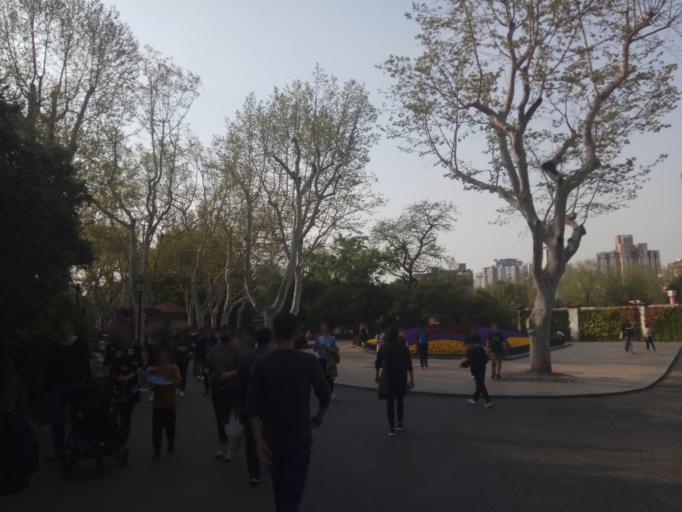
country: CN
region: Shanghai Shi
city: Changning
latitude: 31.2220
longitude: 121.4162
